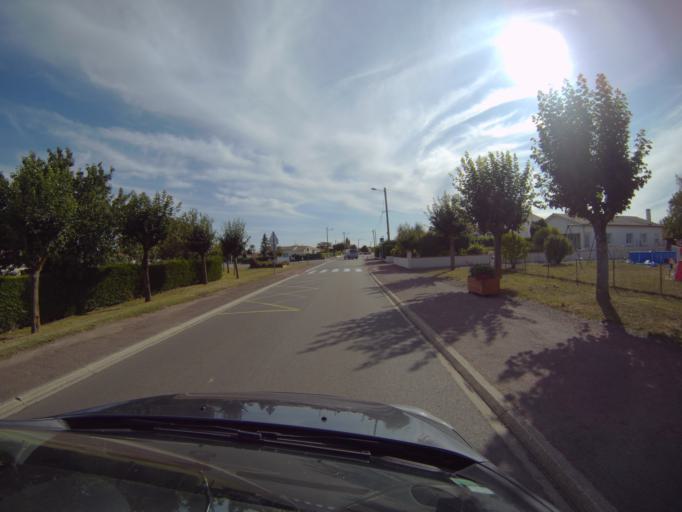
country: FR
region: Pays de la Loire
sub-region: Departement de la Vendee
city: Angles
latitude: 46.4118
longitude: -1.3945
